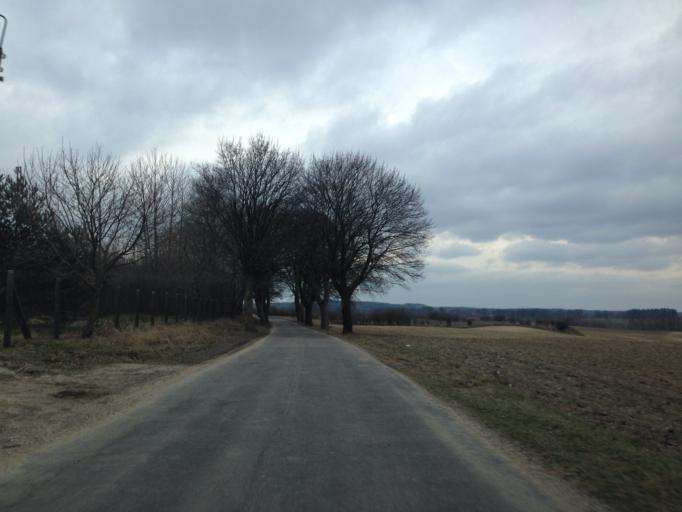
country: PL
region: Kujawsko-Pomorskie
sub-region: Powiat brodnicki
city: Brzozie
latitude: 53.2912
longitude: 19.6832
